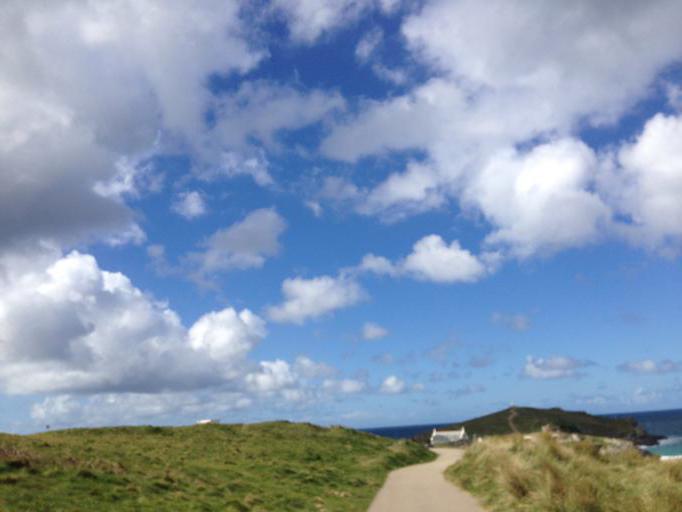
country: GB
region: England
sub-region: Cornwall
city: Newquay
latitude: 50.4208
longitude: -5.0948
